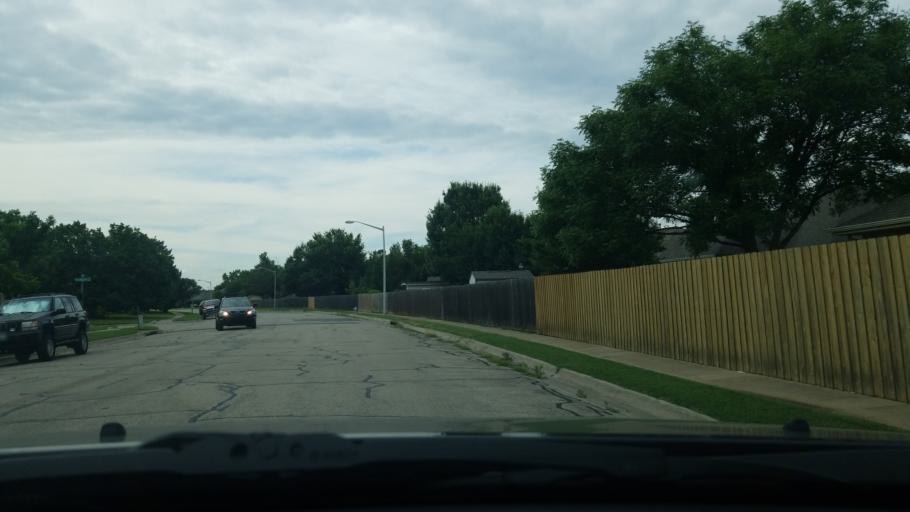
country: US
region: Texas
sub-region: Denton County
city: Denton
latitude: 33.2458
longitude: -97.1270
